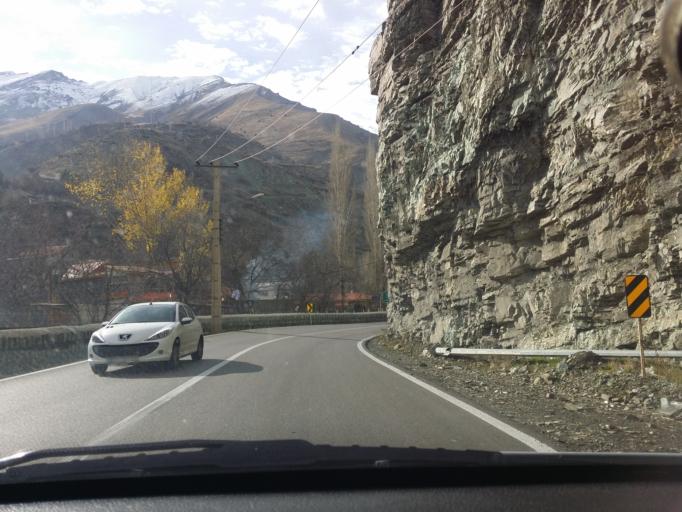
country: IR
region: Alborz
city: Karaj
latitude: 36.0189
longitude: 51.1488
